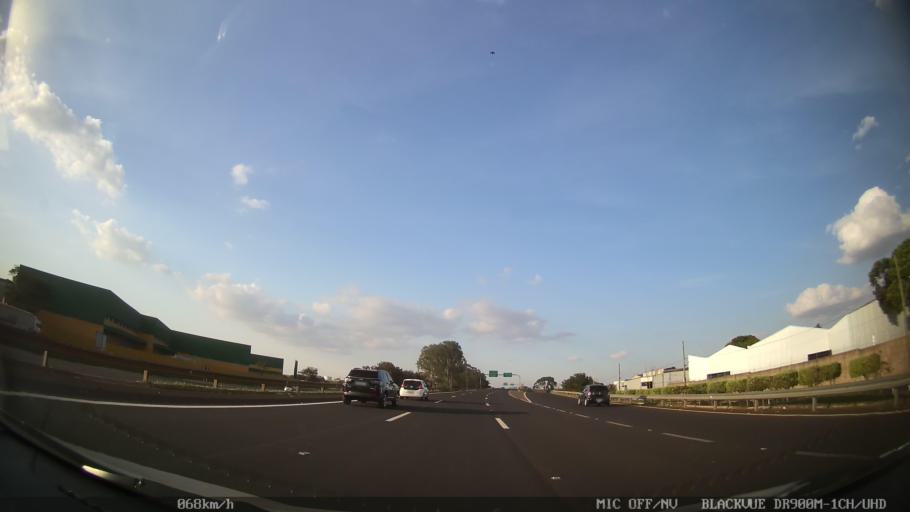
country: BR
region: Sao Paulo
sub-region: Ribeirao Preto
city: Ribeirao Preto
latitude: -21.1164
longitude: -47.7835
